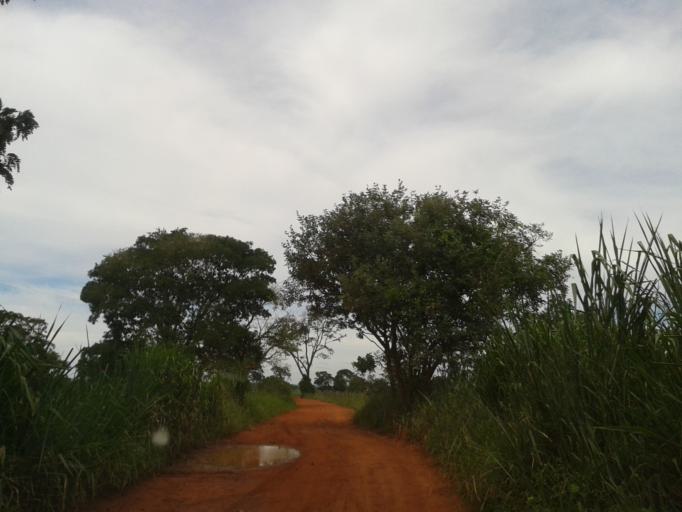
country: BR
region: Minas Gerais
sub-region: Capinopolis
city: Capinopolis
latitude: -18.7936
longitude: -49.8084
